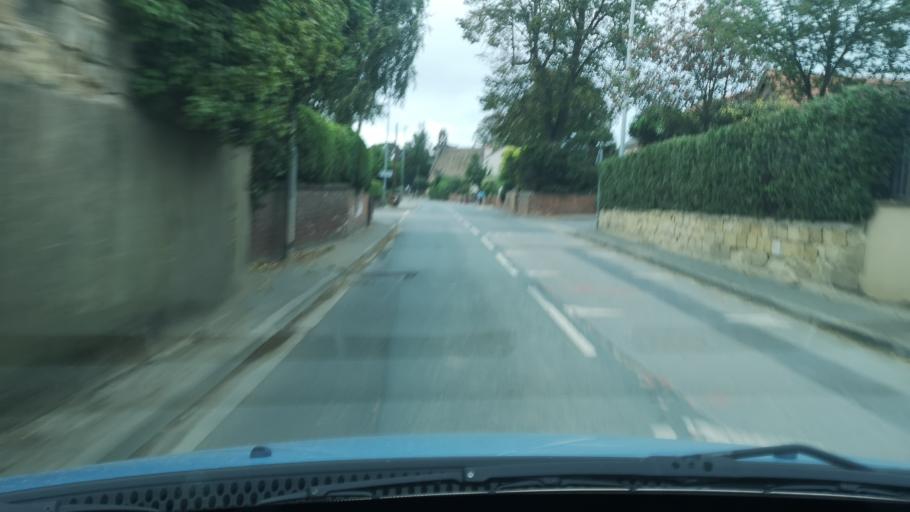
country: GB
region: England
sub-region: City and Borough of Wakefield
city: Darrington
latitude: 53.6752
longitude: -1.2916
